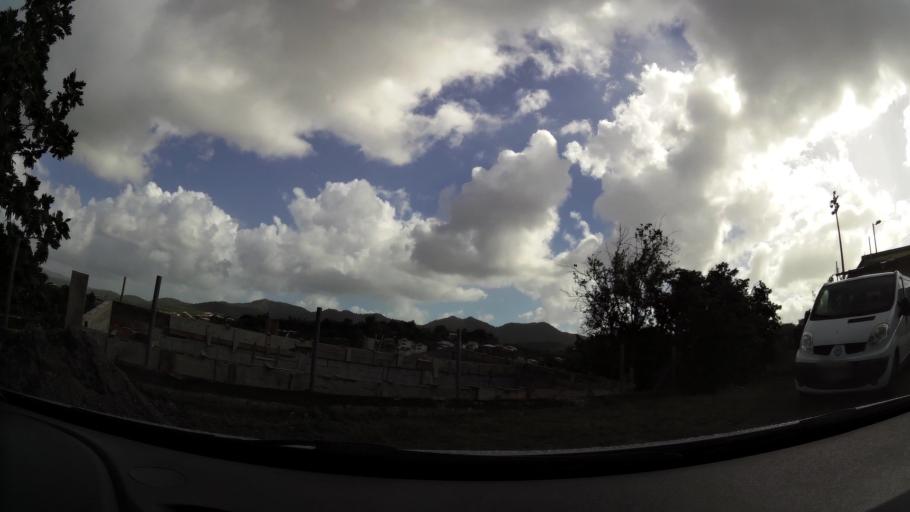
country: MQ
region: Martinique
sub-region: Martinique
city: Les Trois-Ilets
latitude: 14.5379
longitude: -61.0360
